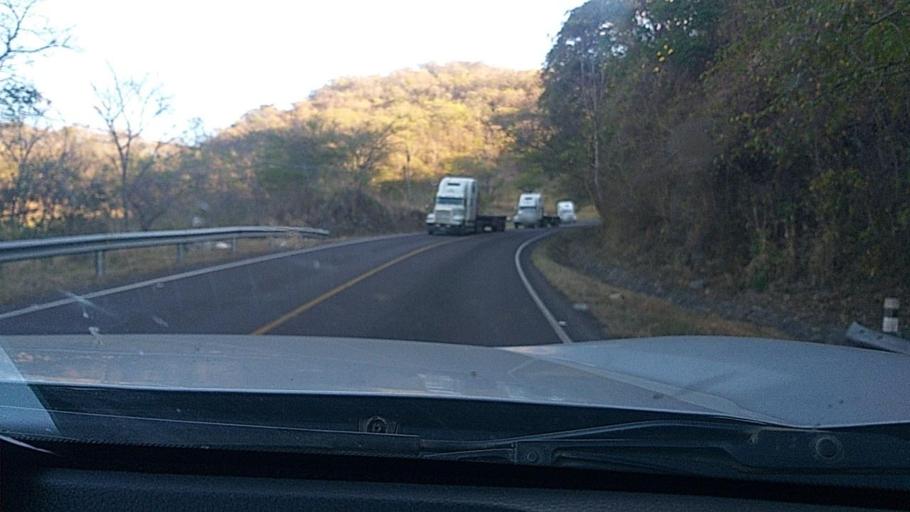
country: NI
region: Esteli
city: Condega
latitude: 13.2586
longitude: -86.3546
